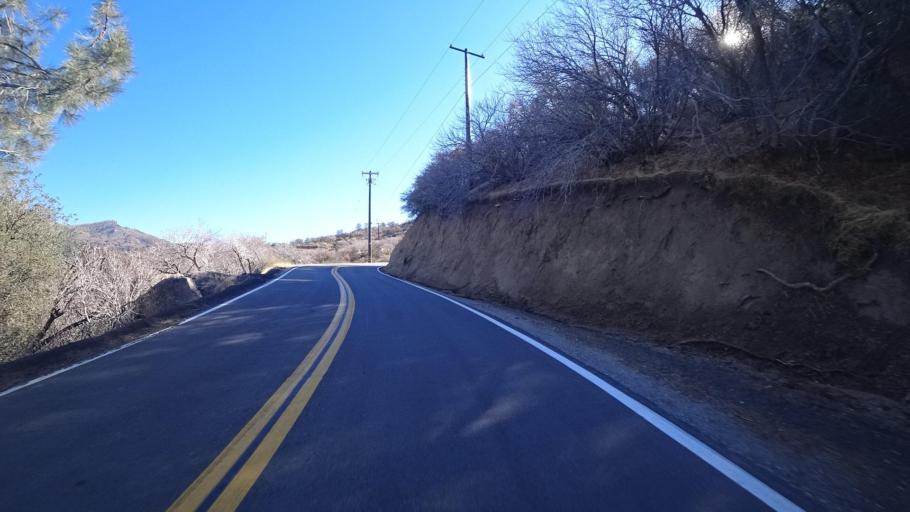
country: US
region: California
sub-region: Kern County
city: Alta Sierra
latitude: 35.7378
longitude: -118.6474
